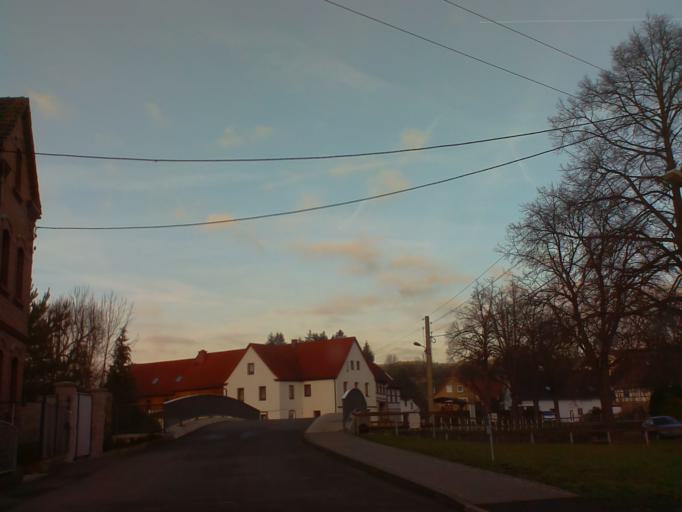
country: DE
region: Thuringia
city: Solkwitz
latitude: 50.7191
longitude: 11.6714
